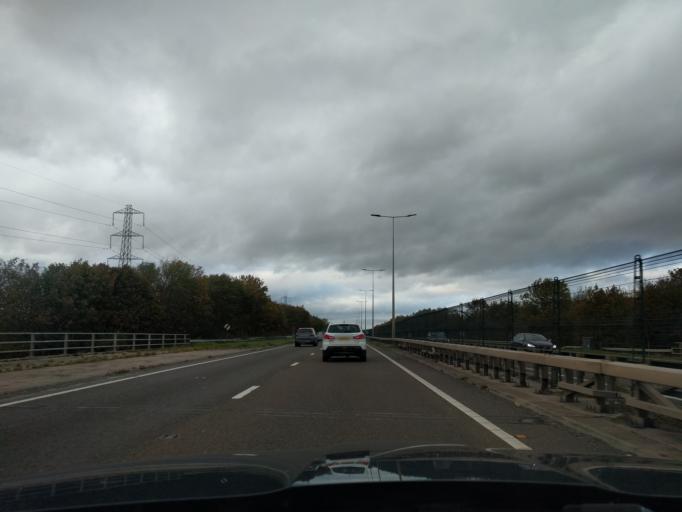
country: GB
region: England
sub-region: Newcastle upon Tyne
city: Hazlerigg
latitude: 55.0414
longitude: -1.6297
